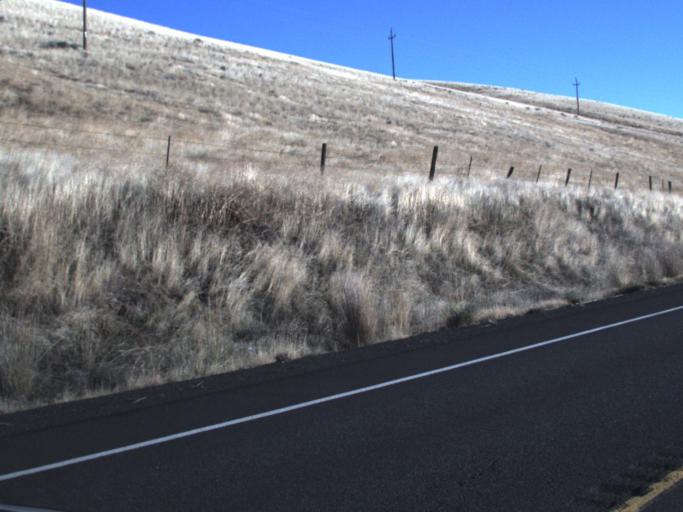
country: US
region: Washington
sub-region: Garfield County
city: Pomeroy
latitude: 46.4679
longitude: -117.4856
